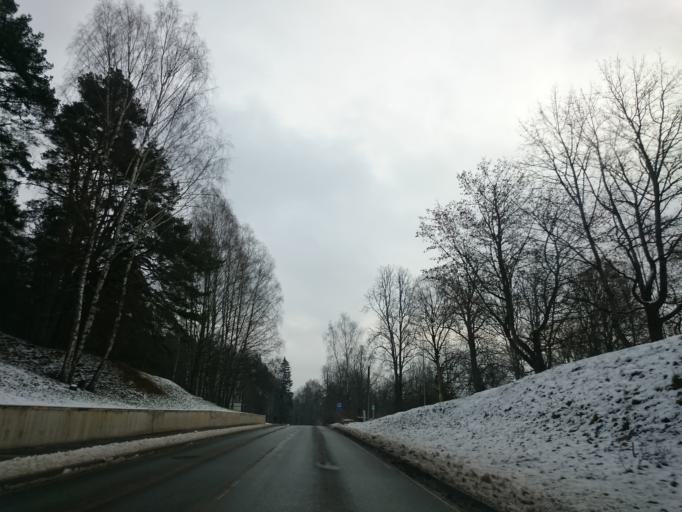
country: LV
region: Cesu Rajons
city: Cesis
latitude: 57.3093
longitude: 25.2313
